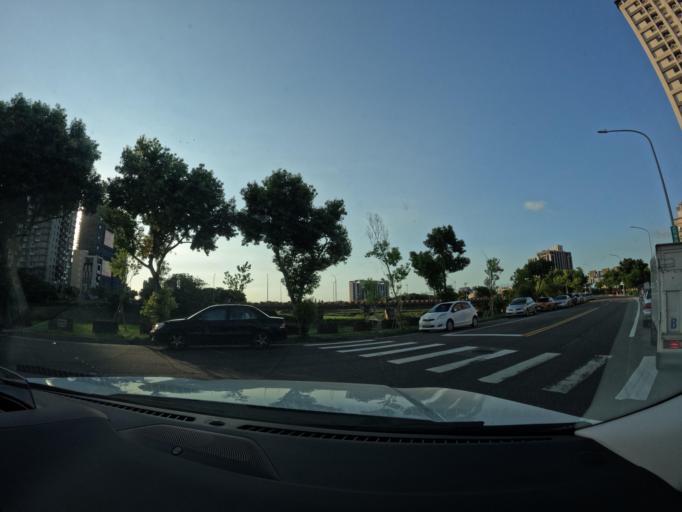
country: TW
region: Taiwan
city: Taoyuan City
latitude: 25.0103
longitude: 121.2105
